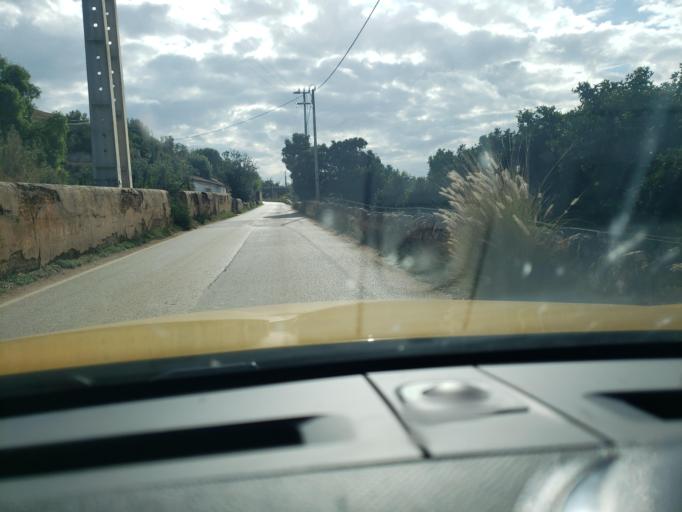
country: PT
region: Faro
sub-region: Portimao
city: Alvor
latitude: 37.1727
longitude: -8.5789
